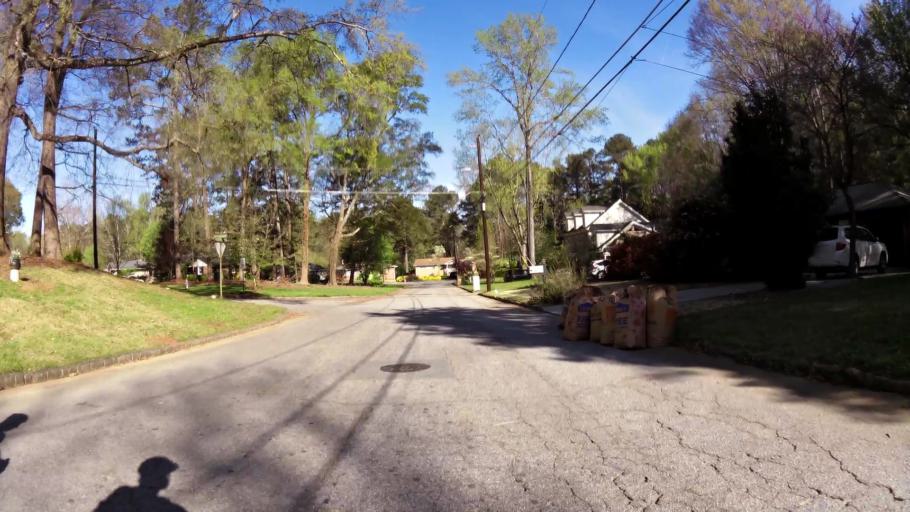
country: US
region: Georgia
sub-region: DeKalb County
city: Clarkston
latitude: 33.8332
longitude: -84.2624
